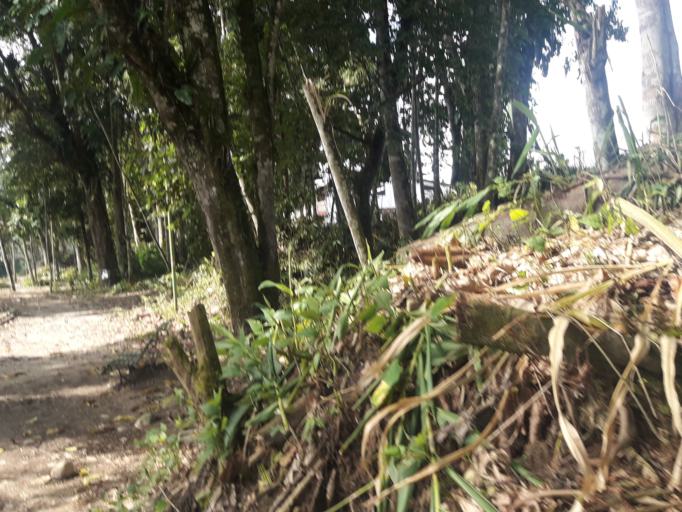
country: EC
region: Napo
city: Tena
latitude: -0.9939
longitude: -77.8188
